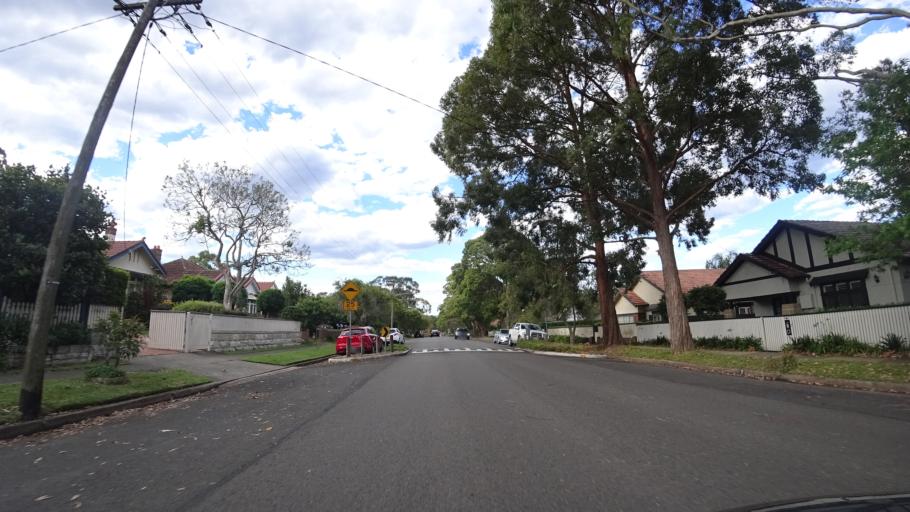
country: AU
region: New South Wales
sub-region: Willoughby
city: Chatswood
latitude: -33.8013
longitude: 151.1917
